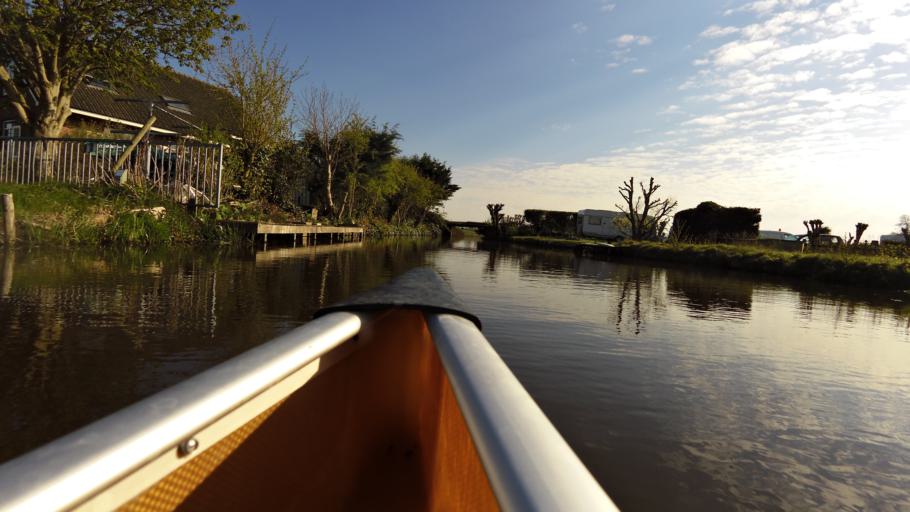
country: NL
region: South Holland
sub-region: Gemeente Teylingen
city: Sassenheim
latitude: 52.2361
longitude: 4.5397
